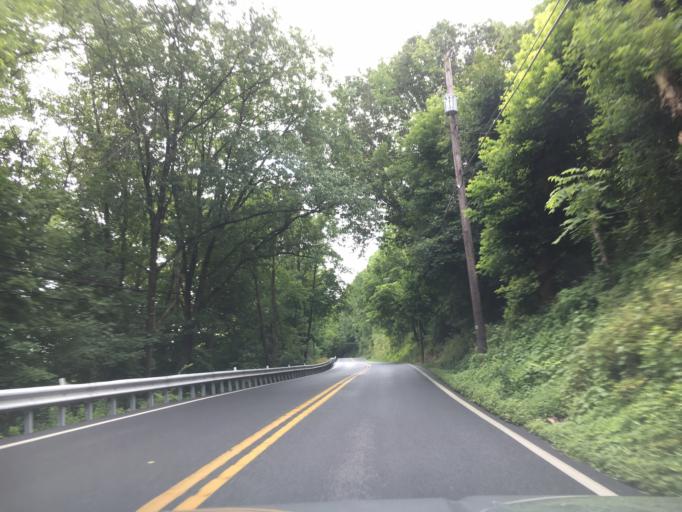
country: US
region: Pennsylvania
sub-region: Lehigh County
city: Cementon
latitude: 40.6981
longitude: -75.5141
